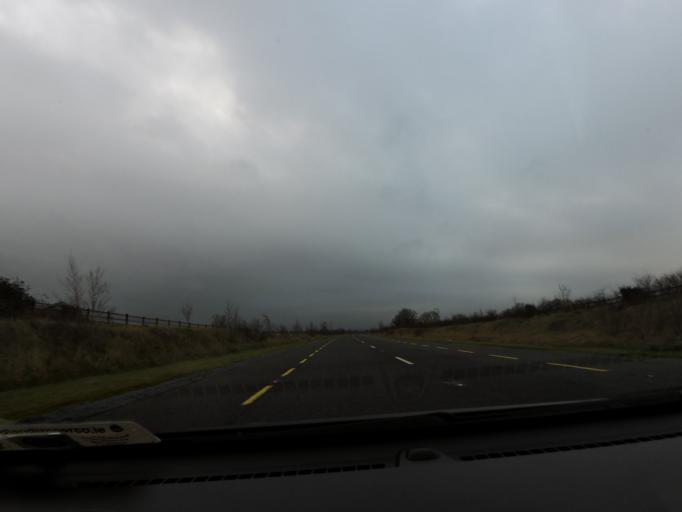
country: IE
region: Connaught
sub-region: County Galway
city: Loughrea
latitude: 53.2470
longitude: -8.5939
